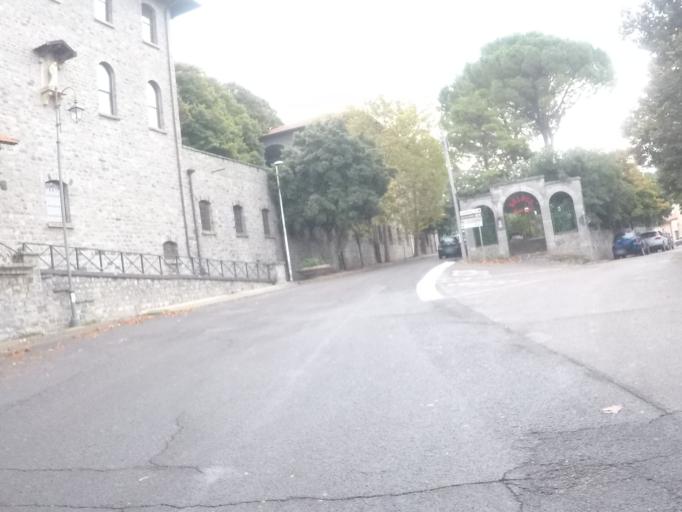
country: IT
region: Sardinia
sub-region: Provincia di Oristano
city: Cuglieri
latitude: 40.1873
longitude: 8.5701
